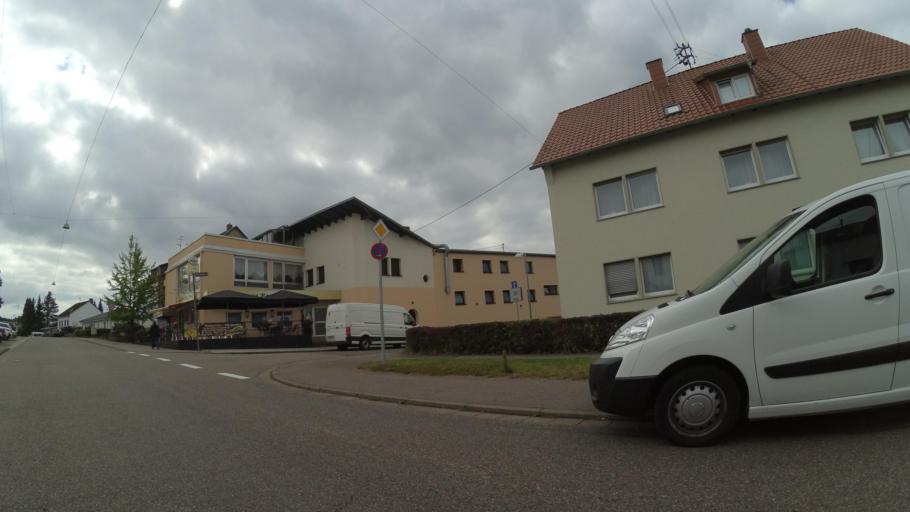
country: FR
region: Lorraine
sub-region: Departement de la Moselle
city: Schoeneck
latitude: 49.2288
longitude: 6.8979
